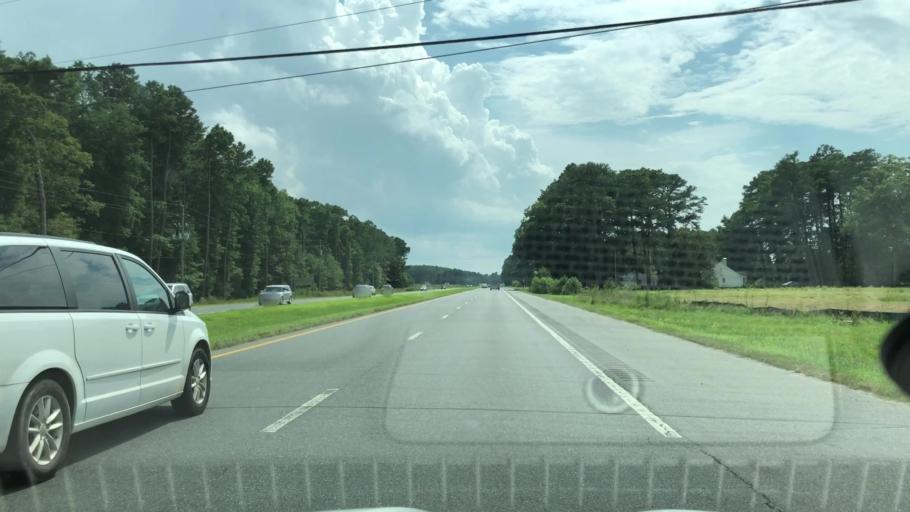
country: US
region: Virginia
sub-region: Accomack County
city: Accomac
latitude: 37.7165
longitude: -75.6892
